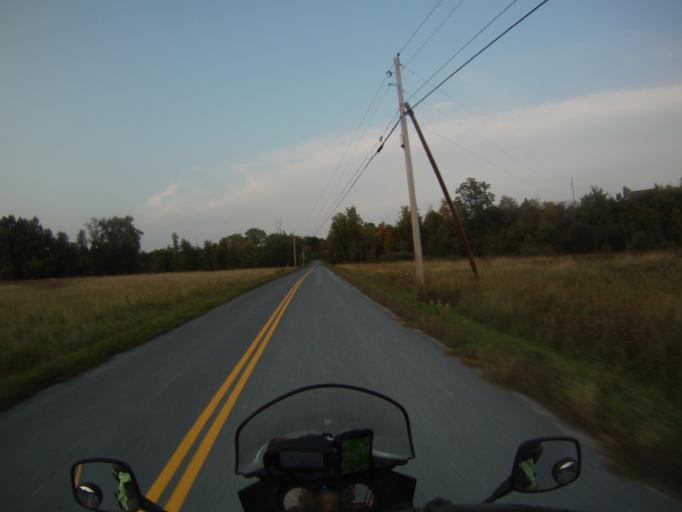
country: US
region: Vermont
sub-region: Rutland County
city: Brandon
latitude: 43.7905
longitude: -73.1102
